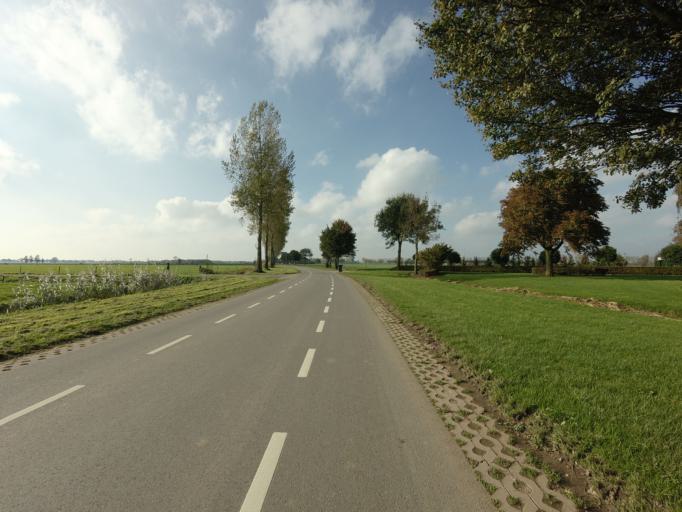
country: NL
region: Gelderland
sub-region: Gemeente Geldermalsen
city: Geldermalsen
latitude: 51.9183
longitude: 5.2993
